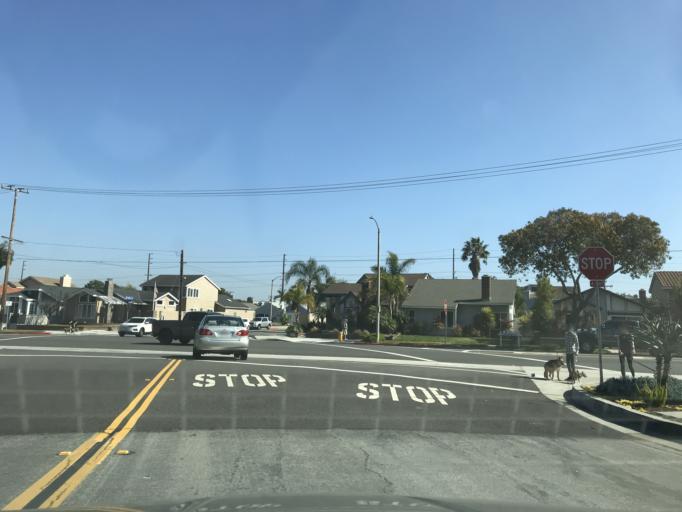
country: US
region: California
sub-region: Orange County
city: Huntington Beach
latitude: 33.6681
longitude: -117.9983
